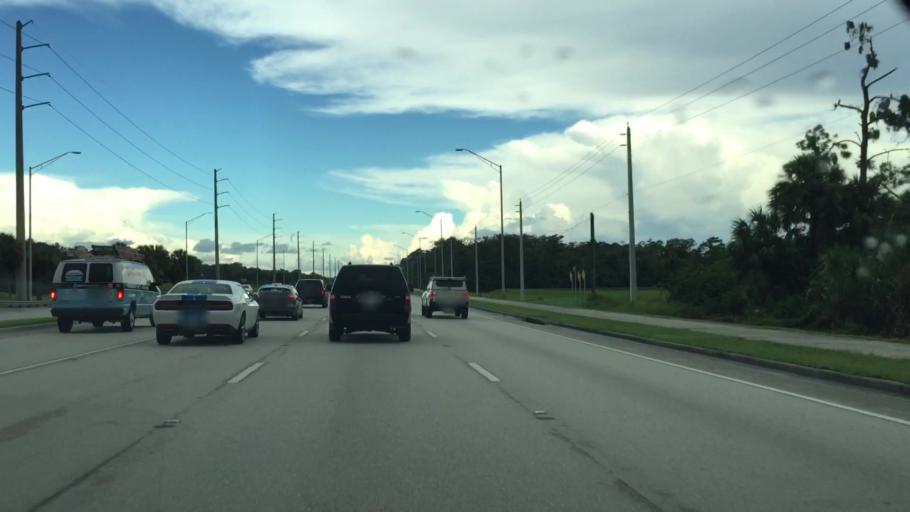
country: US
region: Florida
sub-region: Collier County
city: Orangetree
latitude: 26.2743
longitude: -81.6397
